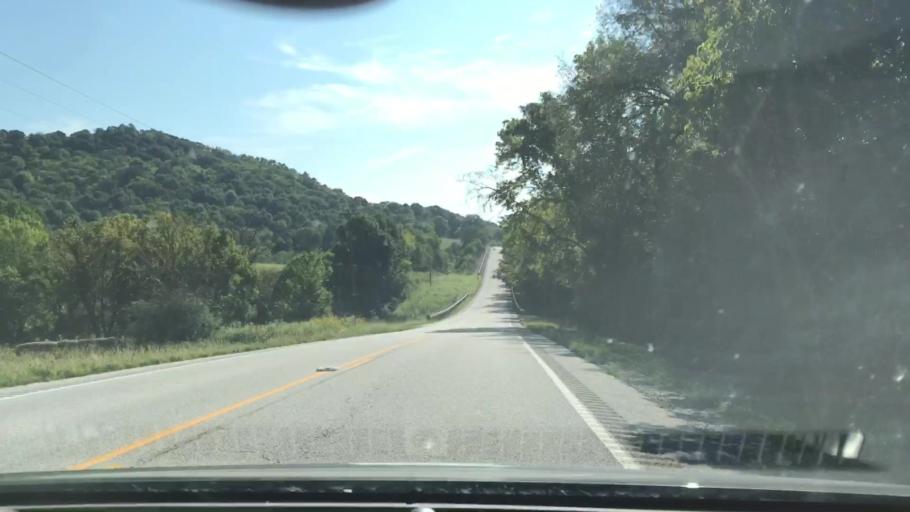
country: US
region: Tennessee
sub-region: Jackson County
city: Gainesboro
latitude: 36.3585
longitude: -85.7379
